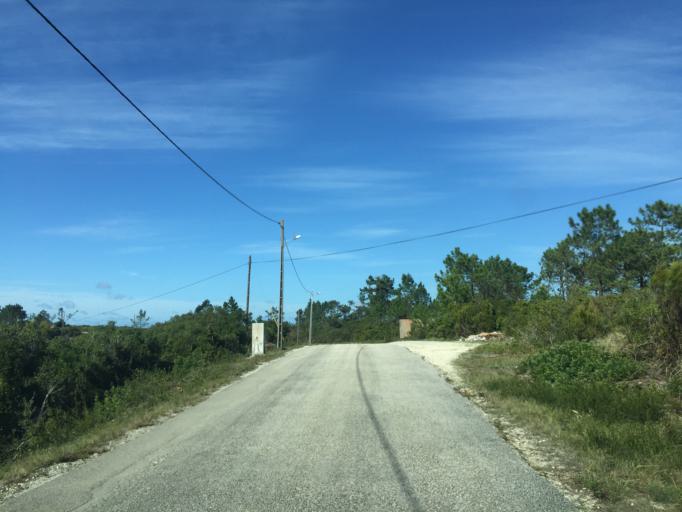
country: PT
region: Coimbra
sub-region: Figueira da Foz
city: Tavarede
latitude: 40.1929
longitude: -8.8429
